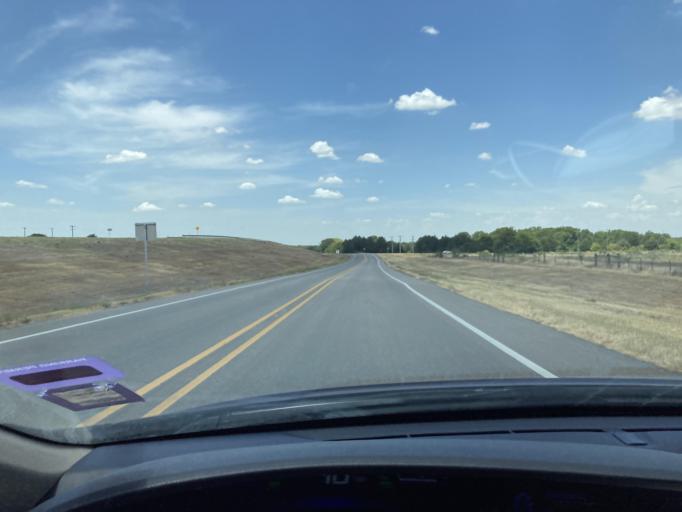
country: US
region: Texas
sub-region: Navarro County
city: Corsicana
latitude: 32.0482
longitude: -96.4937
